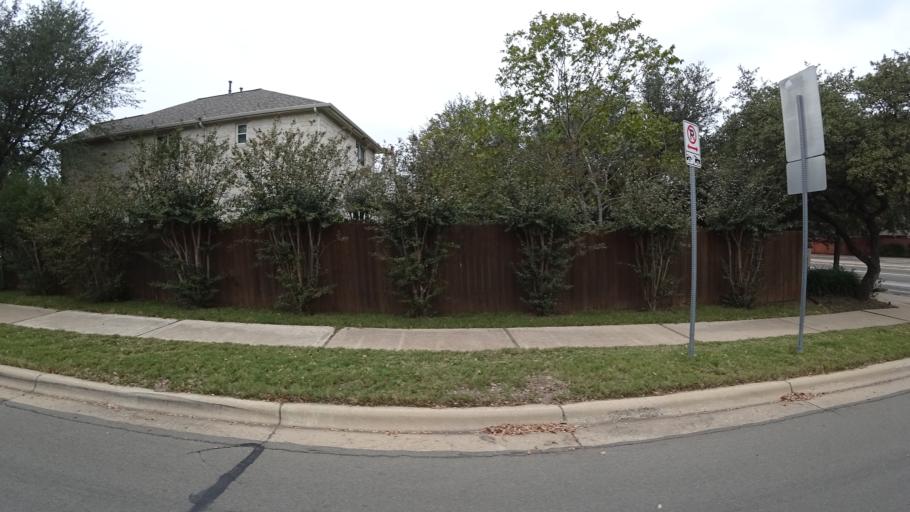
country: US
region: Texas
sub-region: Travis County
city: Shady Hollow
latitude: 30.2119
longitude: -97.8792
